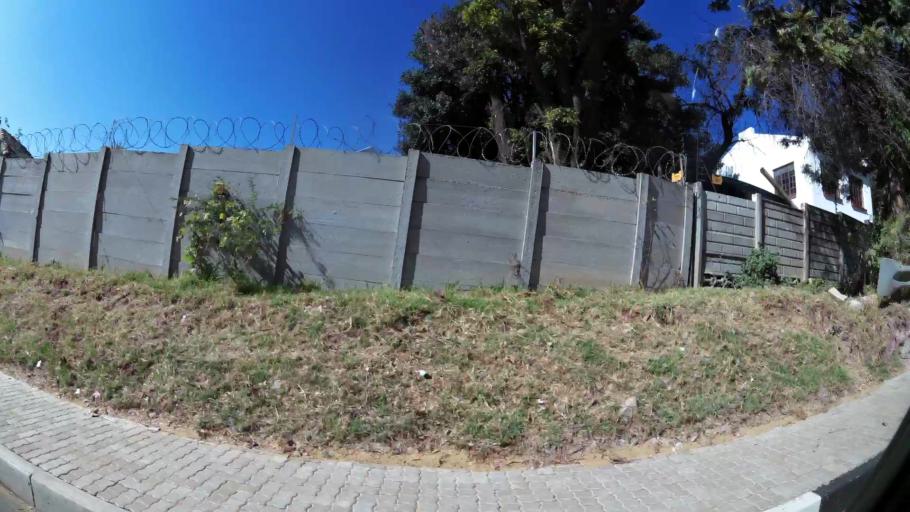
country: ZA
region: Gauteng
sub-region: City of Johannesburg Metropolitan Municipality
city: Roodepoort
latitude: -26.1383
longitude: 27.9098
